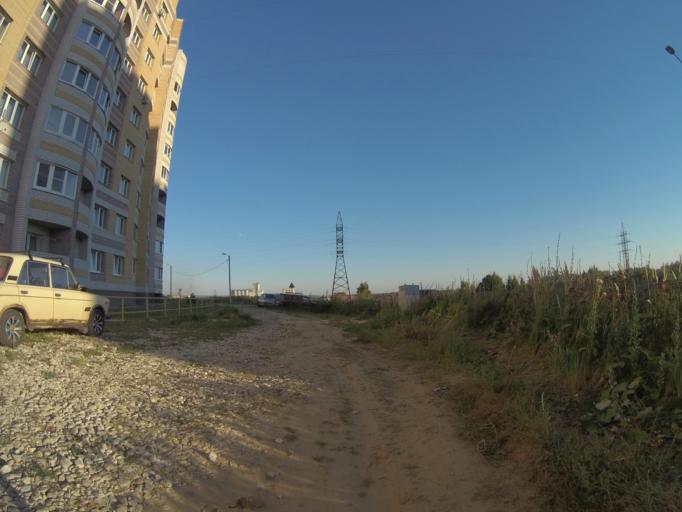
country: RU
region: Vladimir
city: Vladimir
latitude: 56.1042
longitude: 40.3572
